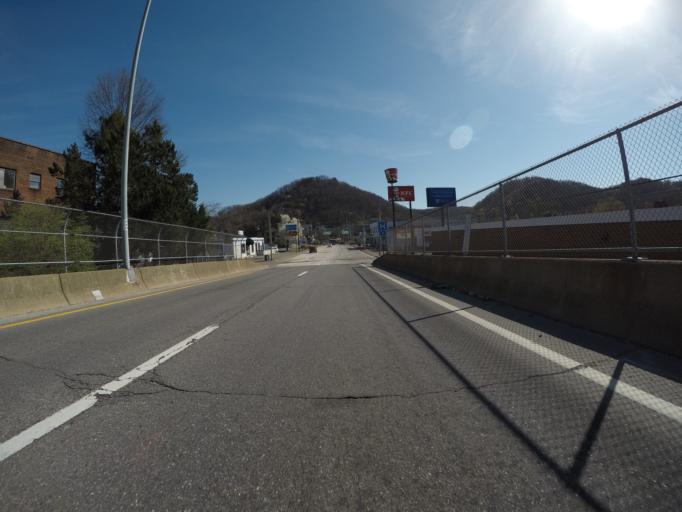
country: US
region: West Virginia
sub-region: Kanawha County
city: Charleston
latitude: 38.3305
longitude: -81.5983
